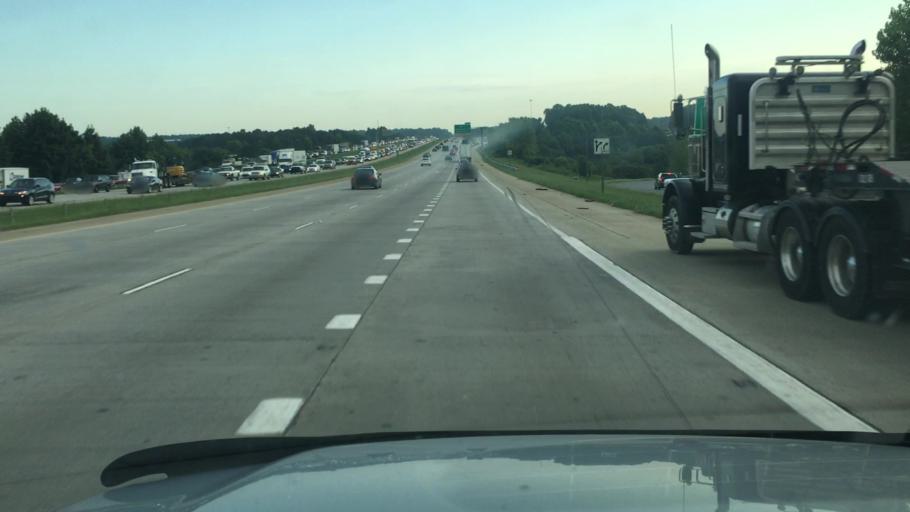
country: US
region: North Carolina
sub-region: Gaston County
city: Belmont
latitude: 35.2324
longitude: -80.9703
